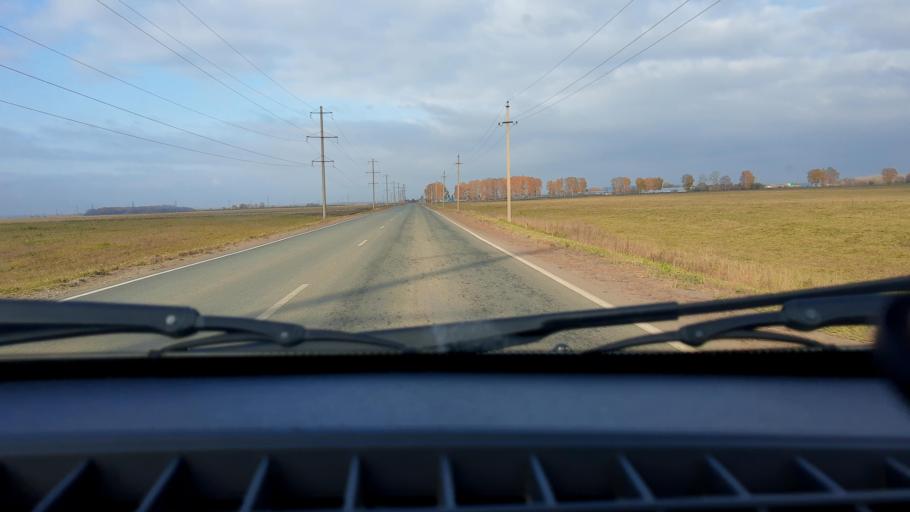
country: RU
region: Bashkortostan
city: Kabakovo
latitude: 54.5411
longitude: 56.0573
